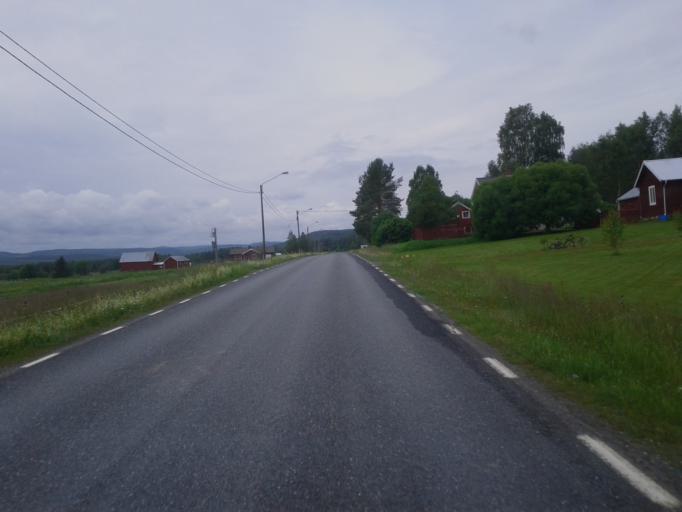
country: SE
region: Vaesterbotten
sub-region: Skelleftea Kommun
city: Forsbacka
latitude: 64.9052
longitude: 20.6385
